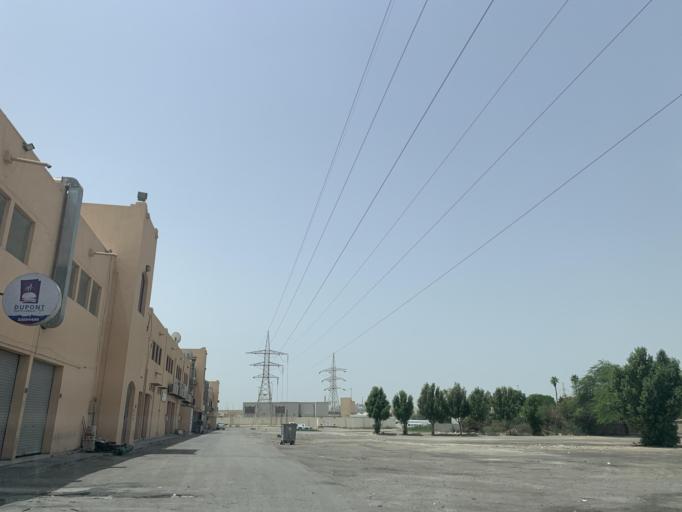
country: BH
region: Northern
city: Sitrah
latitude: 26.1279
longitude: 50.5961
